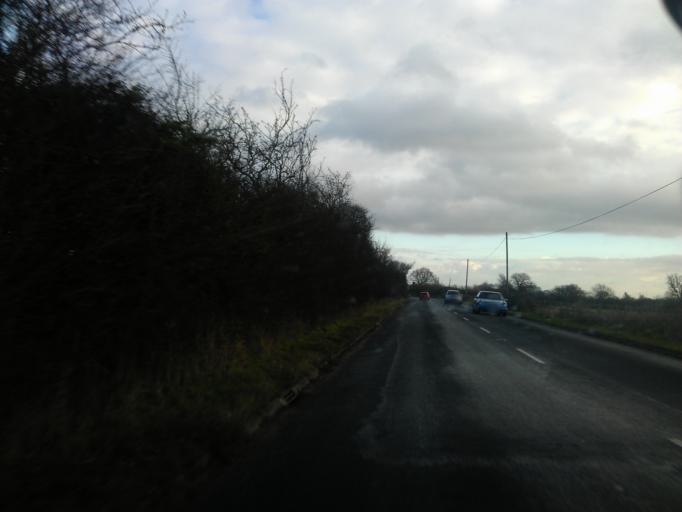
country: GB
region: England
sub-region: Essex
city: Alresford
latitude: 51.8811
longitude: 1.0217
